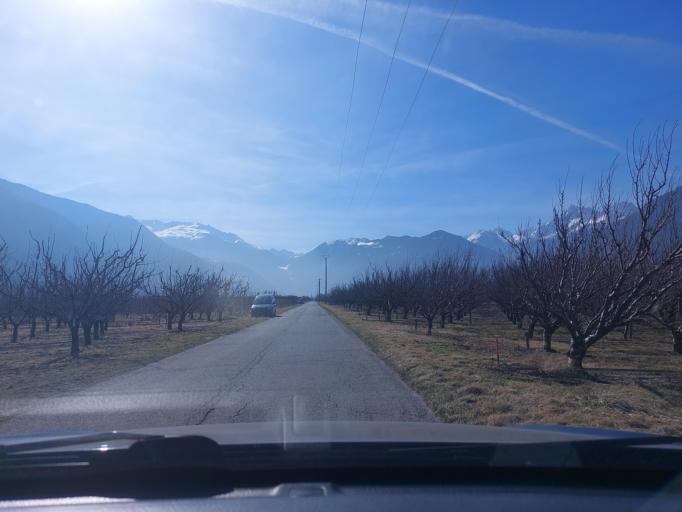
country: CH
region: Valais
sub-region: Martigny District
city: Charrat-les-Chenes
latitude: 46.1343
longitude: 7.1464
